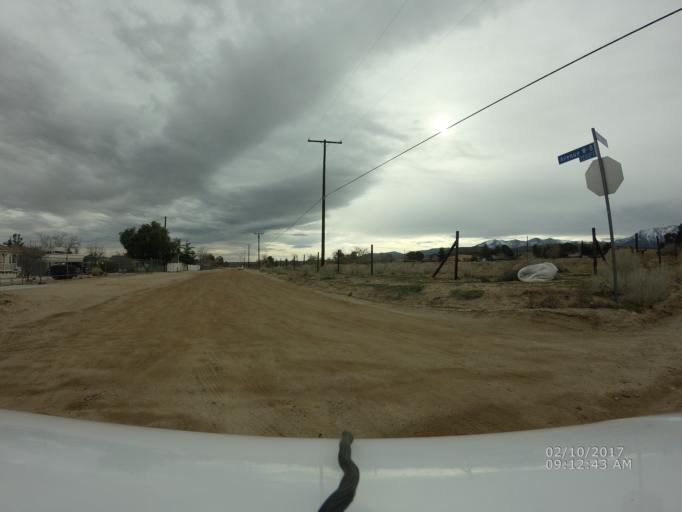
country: US
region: California
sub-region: Los Angeles County
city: Littlerock
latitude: 34.4918
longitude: -117.8944
